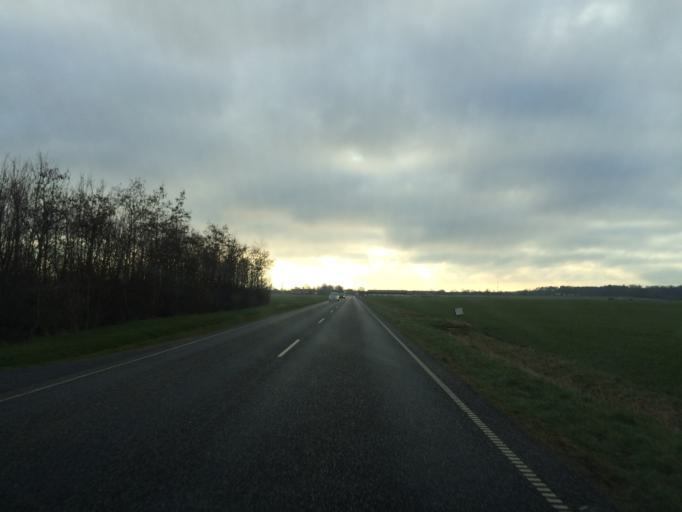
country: DK
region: South Denmark
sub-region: Fredericia Kommune
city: Snoghoj
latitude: 55.5694
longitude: 9.6778
